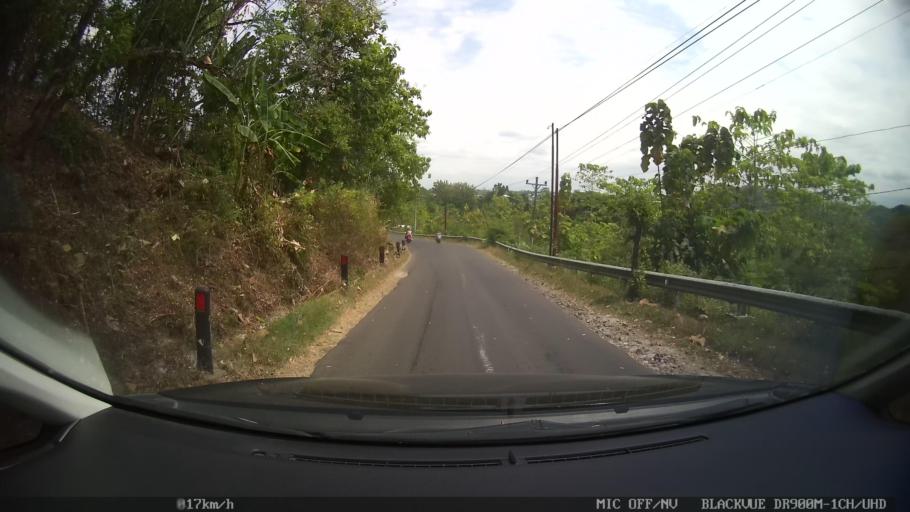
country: ID
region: Central Java
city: Candi Prambanan
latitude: -7.7835
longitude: 110.4926
